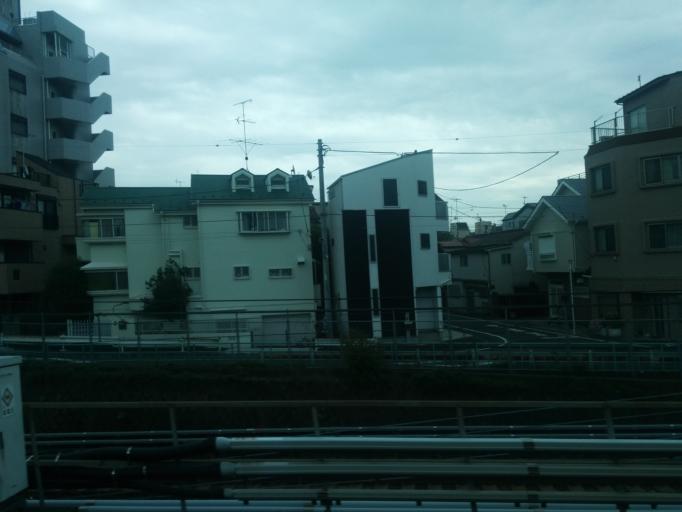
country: JP
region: Tokyo
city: Tokyo
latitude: 35.7388
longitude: 139.7522
